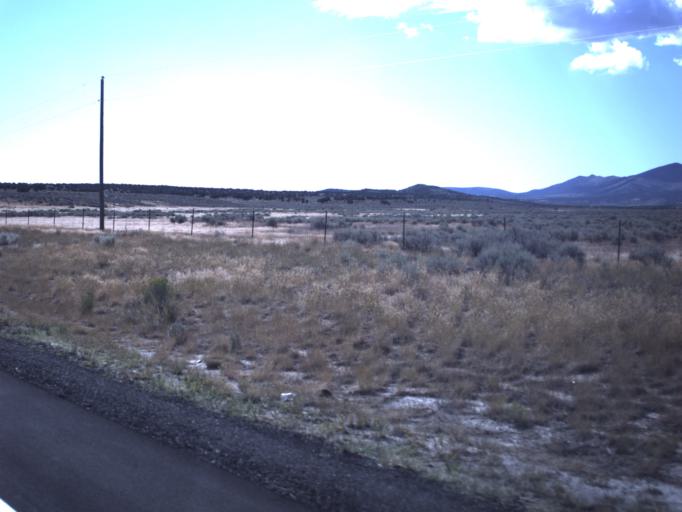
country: US
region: Utah
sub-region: Utah County
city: Eagle Mountain
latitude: 40.0733
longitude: -112.3368
